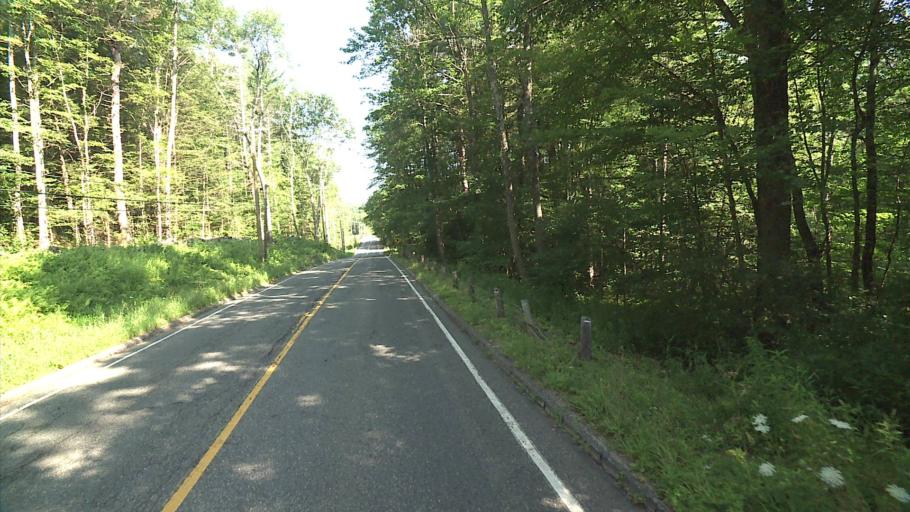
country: US
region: Connecticut
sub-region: Litchfield County
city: Winsted
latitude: 42.0120
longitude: -73.1109
